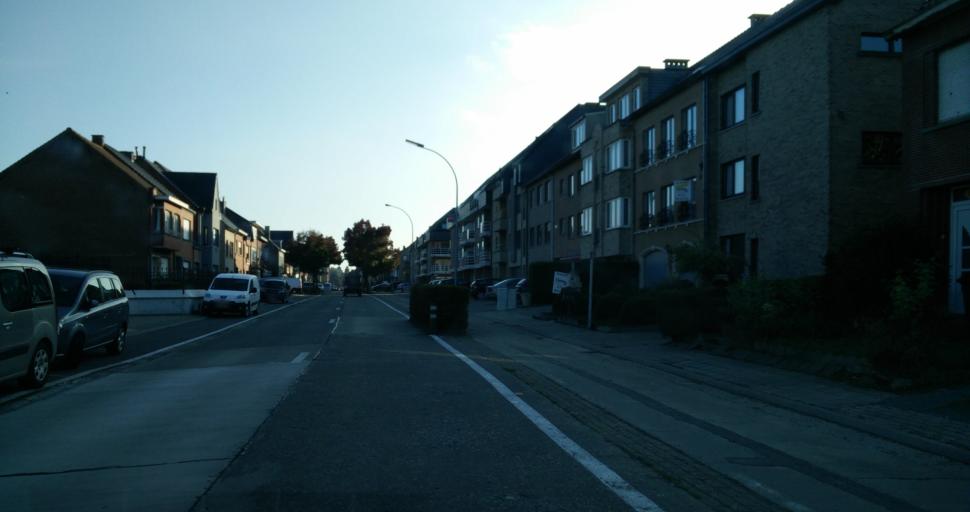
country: BE
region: Flanders
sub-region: Provincie Oost-Vlaanderen
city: Ninove
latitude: 50.8466
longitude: 4.0210
